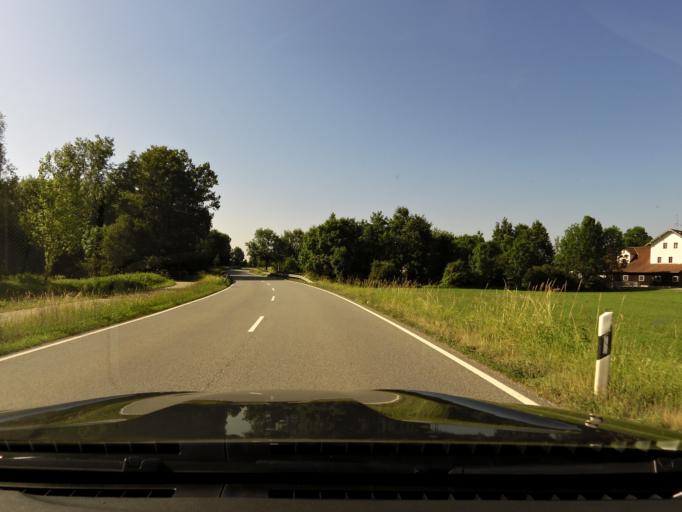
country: DE
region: Bavaria
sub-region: Upper Bavaria
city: Rohrbach
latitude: 48.2806
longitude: 12.5530
